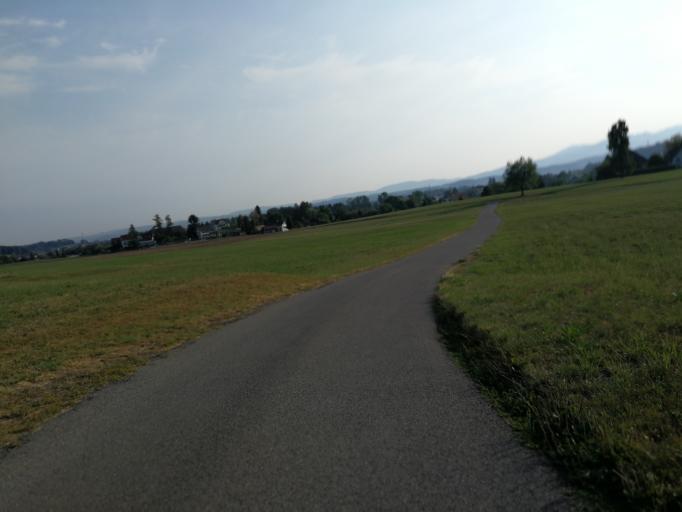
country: CH
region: Zurich
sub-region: Bezirk Uster
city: Esslingen
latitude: 47.2780
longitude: 8.7139
